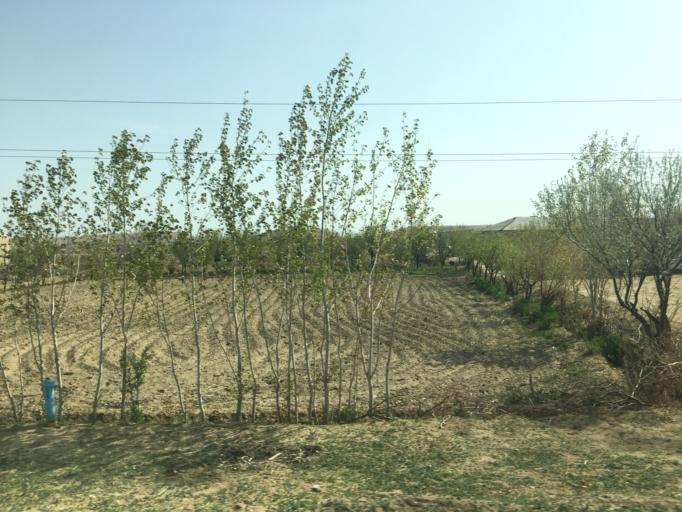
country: TM
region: Mary
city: Seydi
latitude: 39.4104
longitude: 63.0001
